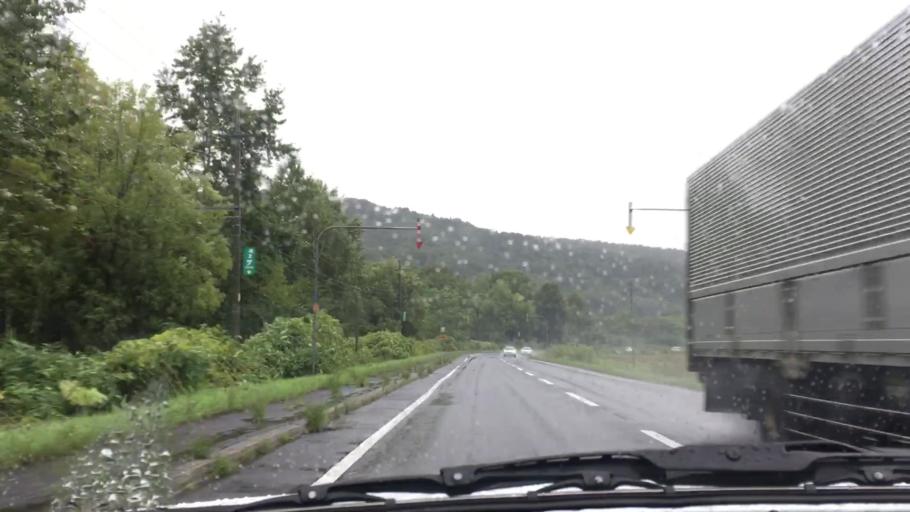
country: JP
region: Hokkaido
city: Niseko Town
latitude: 42.8029
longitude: 140.9917
